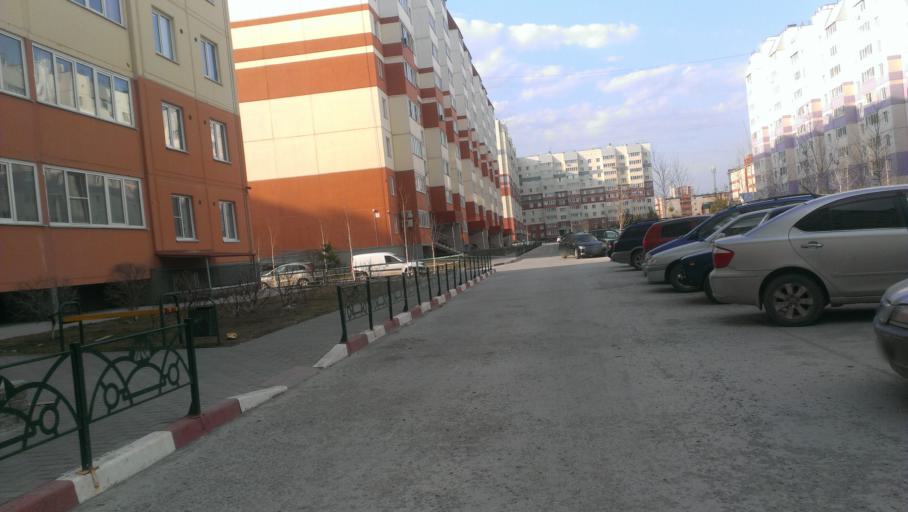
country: RU
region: Altai Krai
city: Novosilikatnyy
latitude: 53.3258
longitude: 83.6755
